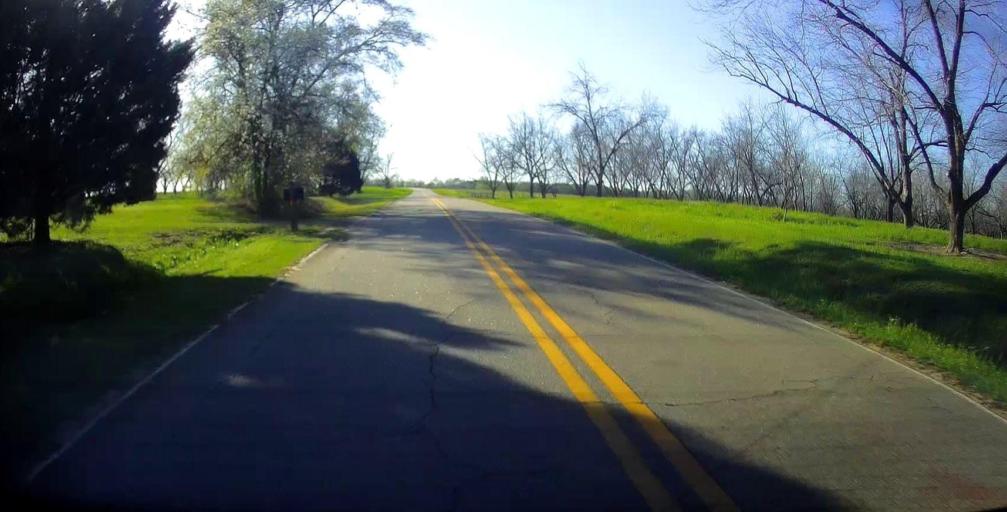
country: US
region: Georgia
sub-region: Houston County
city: Perry
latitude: 32.3671
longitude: -83.6839
